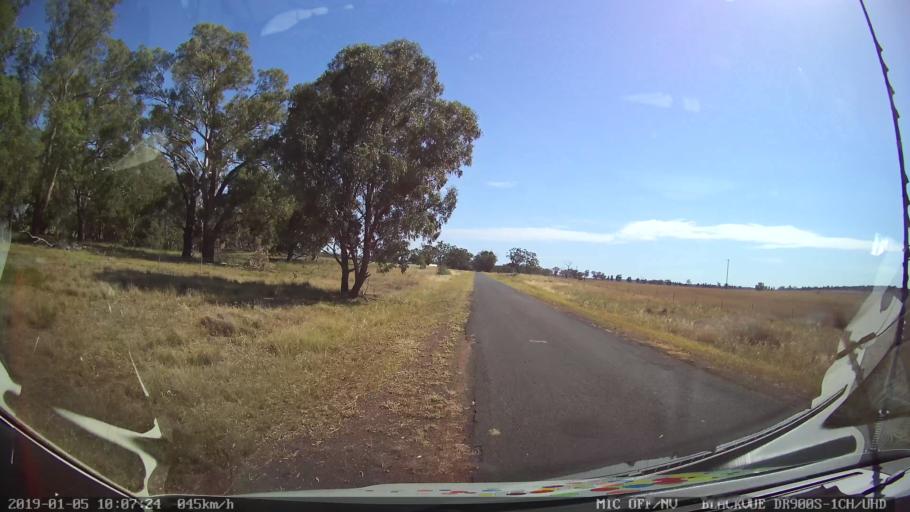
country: AU
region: New South Wales
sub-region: Gilgandra
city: Gilgandra
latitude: -31.6500
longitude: 148.8744
